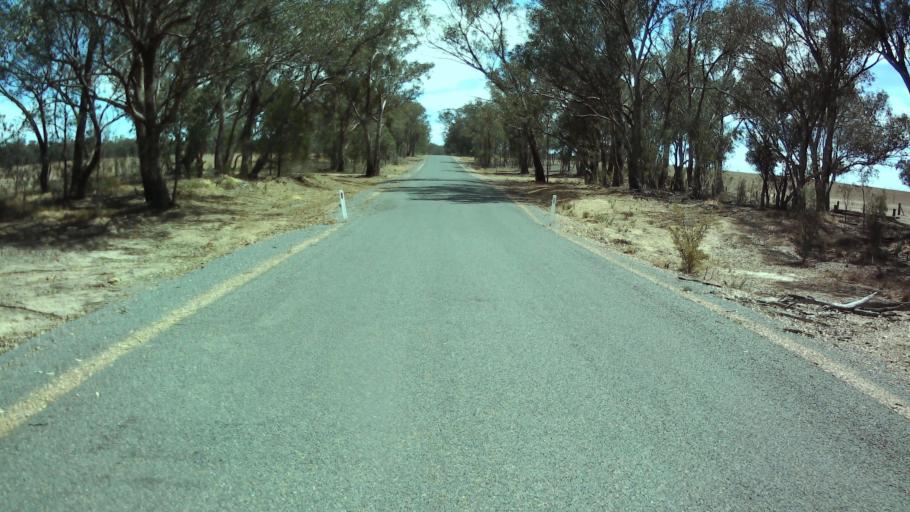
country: AU
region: New South Wales
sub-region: Weddin
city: Grenfell
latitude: -33.7369
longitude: 148.2087
